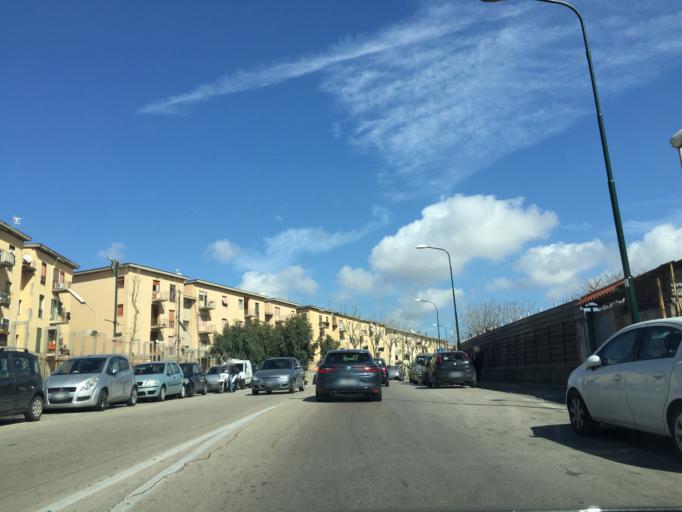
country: IT
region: Campania
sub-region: Provincia di Napoli
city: Portici
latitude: 40.8221
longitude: 14.3248
